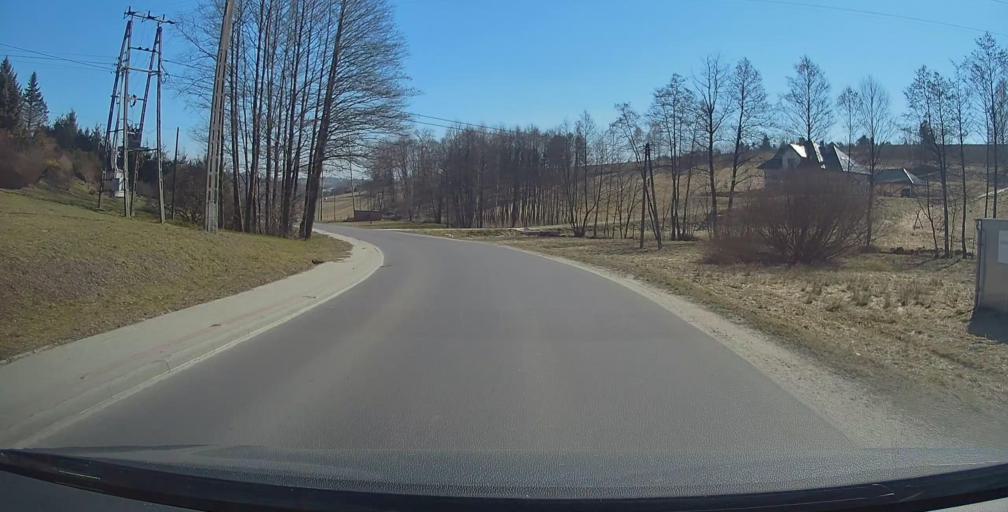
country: PL
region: Subcarpathian Voivodeship
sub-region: Powiat rzeszowski
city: Hyzne
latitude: 49.8880
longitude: 22.2283
